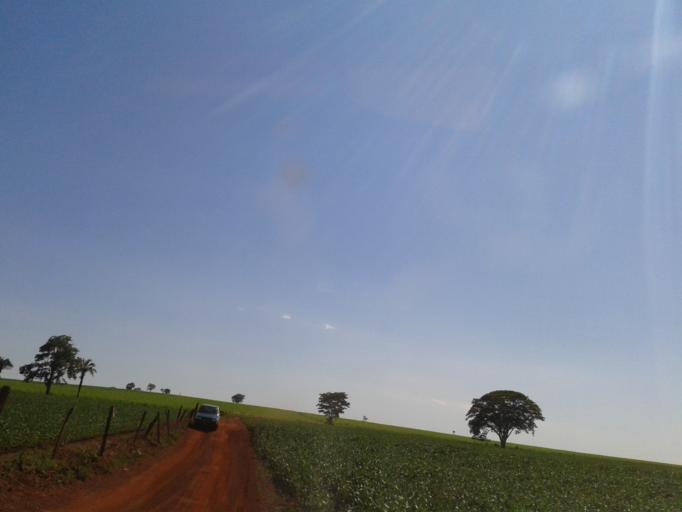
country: BR
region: Minas Gerais
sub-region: Centralina
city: Centralina
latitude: -18.6173
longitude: -49.2868
